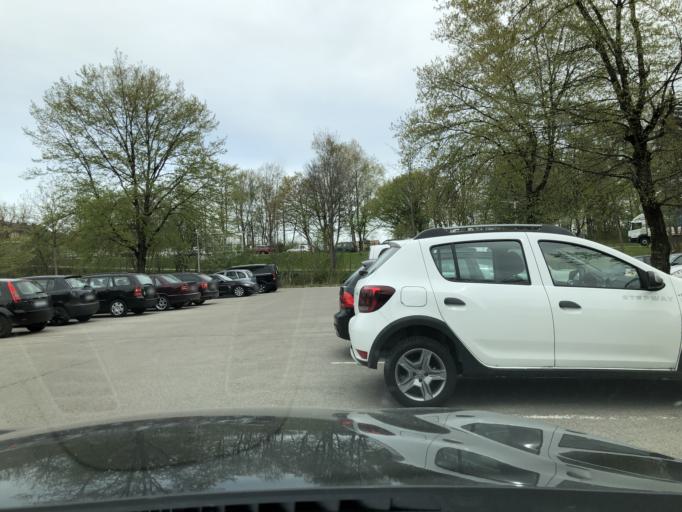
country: DE
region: Bavaria
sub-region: Swabia
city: Fuessen
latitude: 47.5677
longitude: 10.7047
